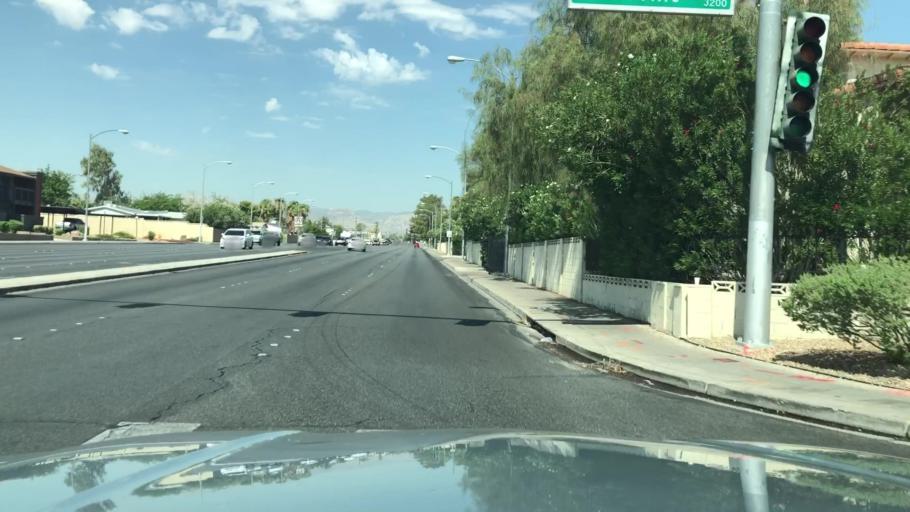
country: US
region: Nevada
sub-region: Clark County
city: Spring Valley
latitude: 36.1301
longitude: -115.1993
